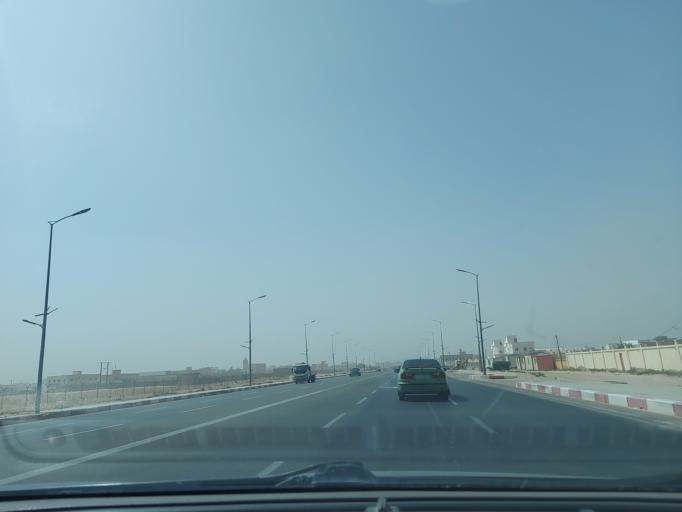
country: MR
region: Nouakchott
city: Nouakchott
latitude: 18.1344
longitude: -16.0046
